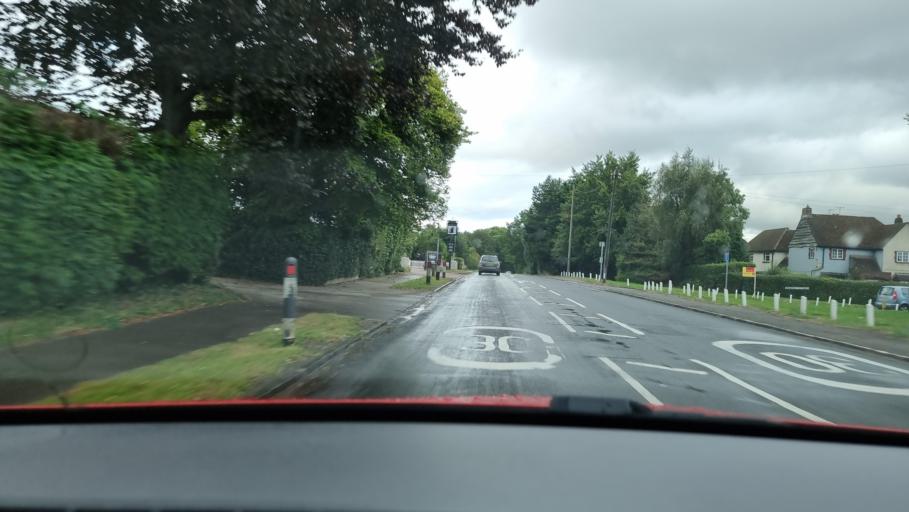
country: GB
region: England
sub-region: Hertfordshire
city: Berkhamsted
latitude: 51.7385
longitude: -0.5868
